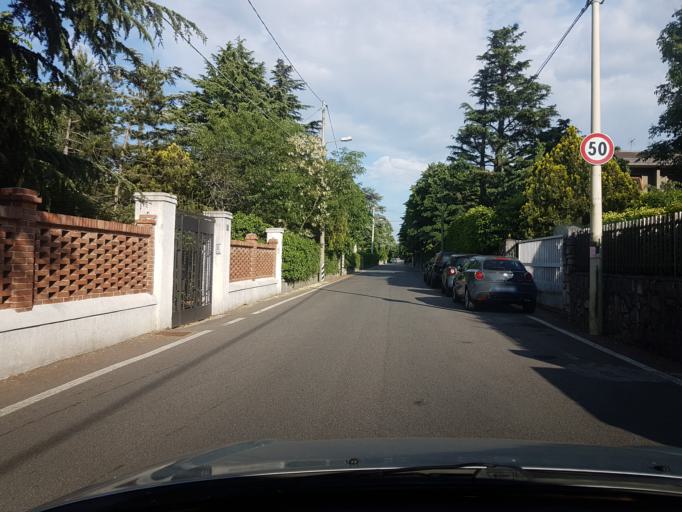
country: IT
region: Friuli Venezia Giulia
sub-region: Provincia di Trieste
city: Villa Opicina
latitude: 45.6876
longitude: 13.7805
